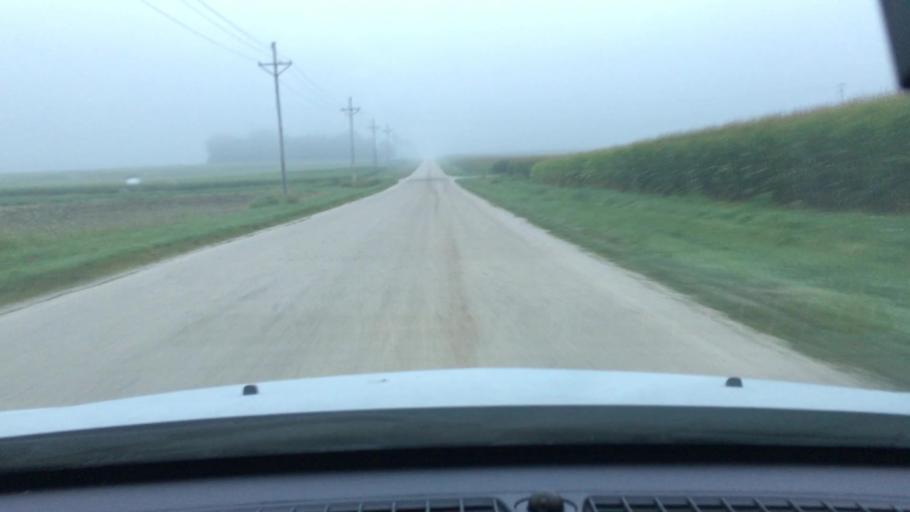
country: US
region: Illinois
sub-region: Ogle County
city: Rochelle
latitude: 41.8986
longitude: -88.9818
